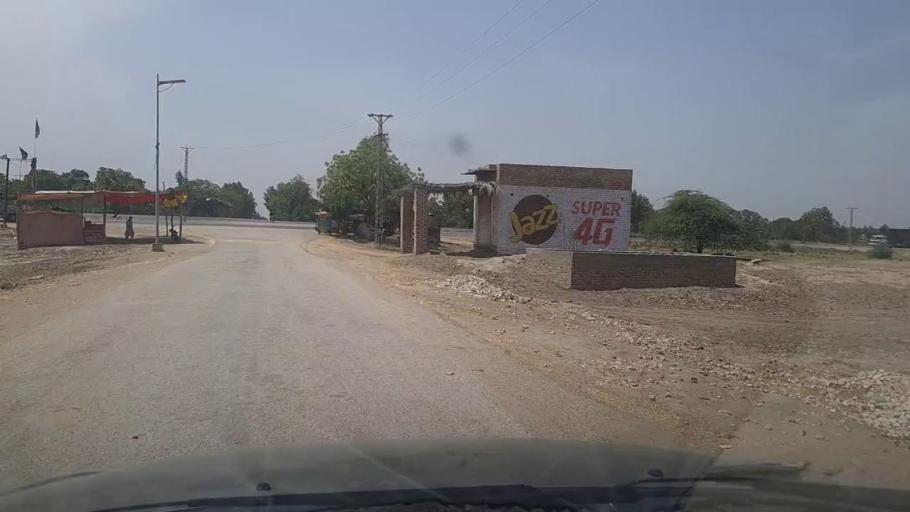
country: PK
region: Sindh
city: Bhiria
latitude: 26.9113
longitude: 68.1874
